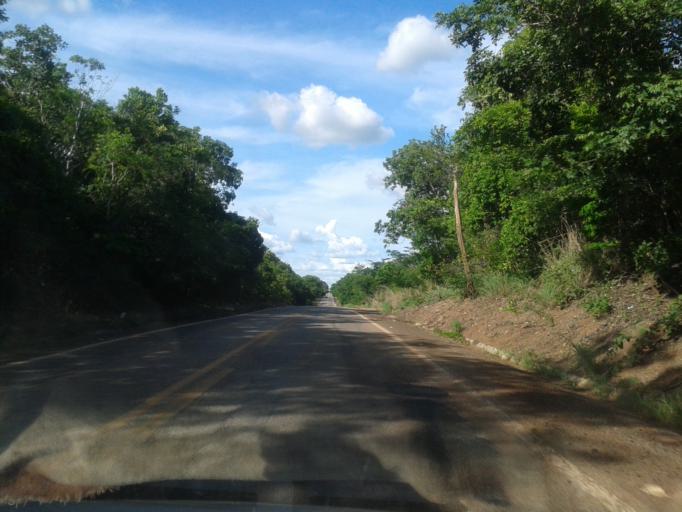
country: BR
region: Goias
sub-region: Mozarlandia
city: Mozarlandia
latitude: -14.6906
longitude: -50.5428
